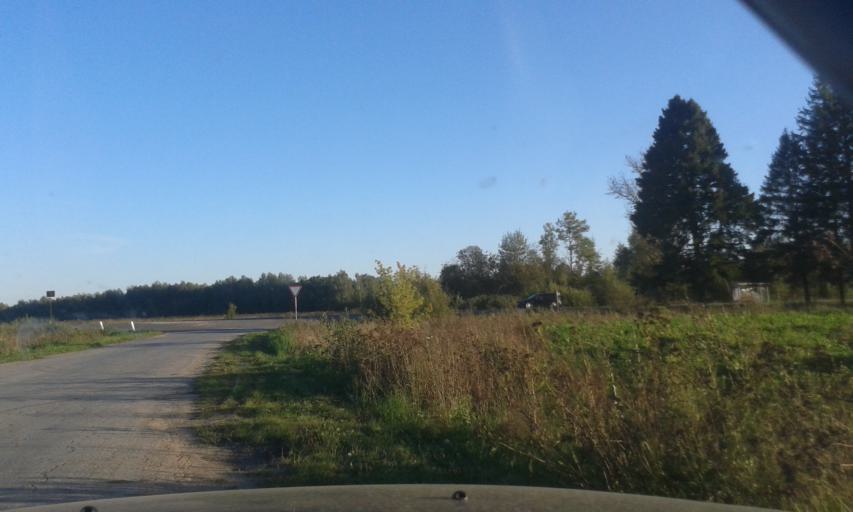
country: RU
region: Tula
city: Krapivna
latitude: 54.1149
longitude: 37.1528
